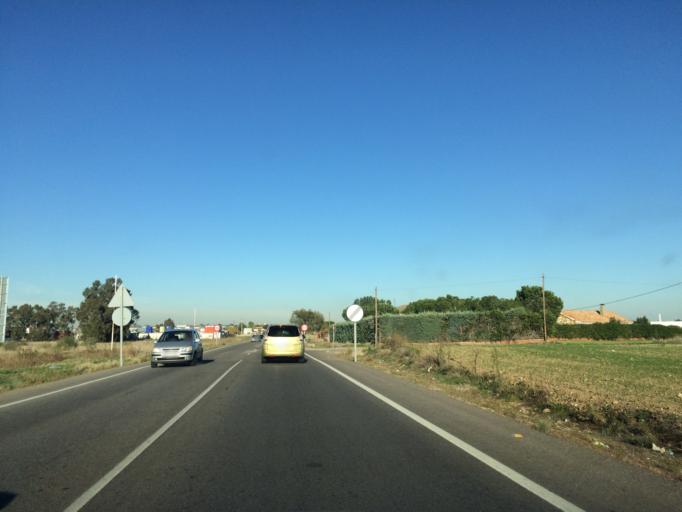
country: ES
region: Madrid
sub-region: Provincia de Madrid
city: Serranillos del Valle
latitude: 40.1864
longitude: -3.8816
